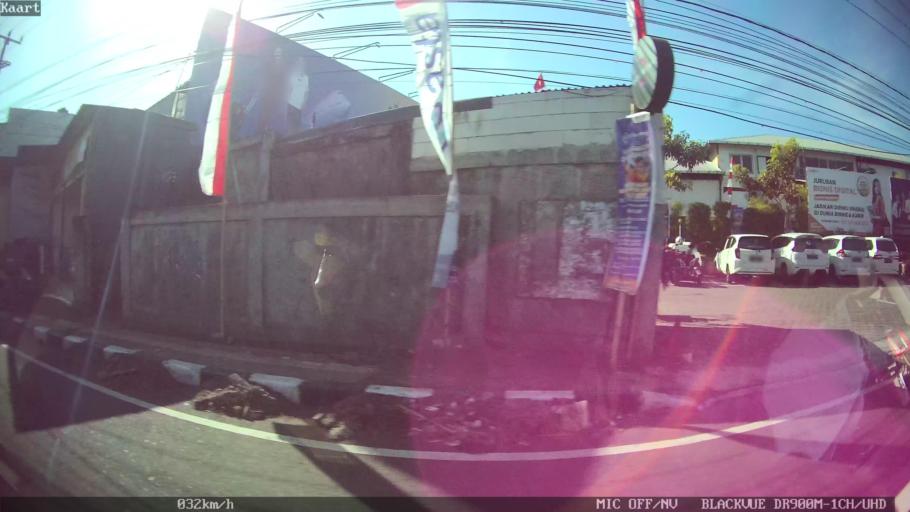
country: ID
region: Bali
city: Banjar Kertasari
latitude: -8.6182
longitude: 115.1924
